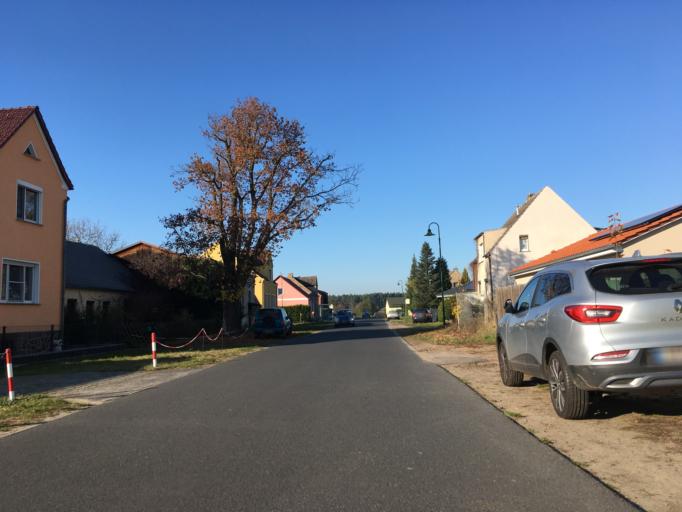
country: DE
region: Brandenburg
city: Rauen
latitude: 52.3368
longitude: 13.9474
